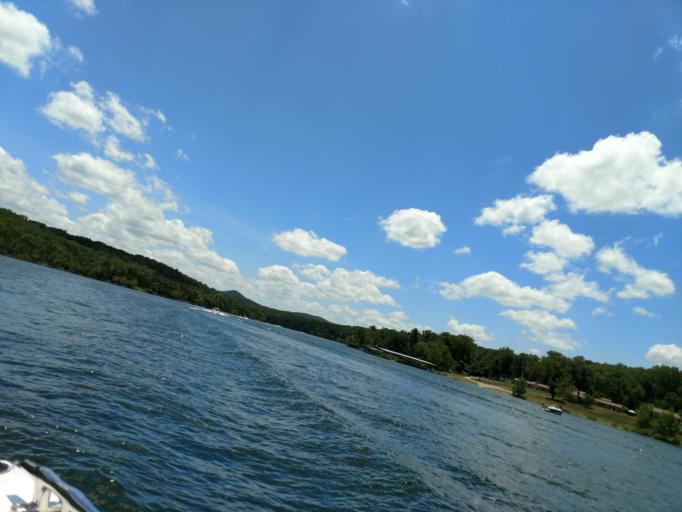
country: US
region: Missouri
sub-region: Barry County
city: Shell Knob
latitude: 36.5811
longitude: -93.5675
